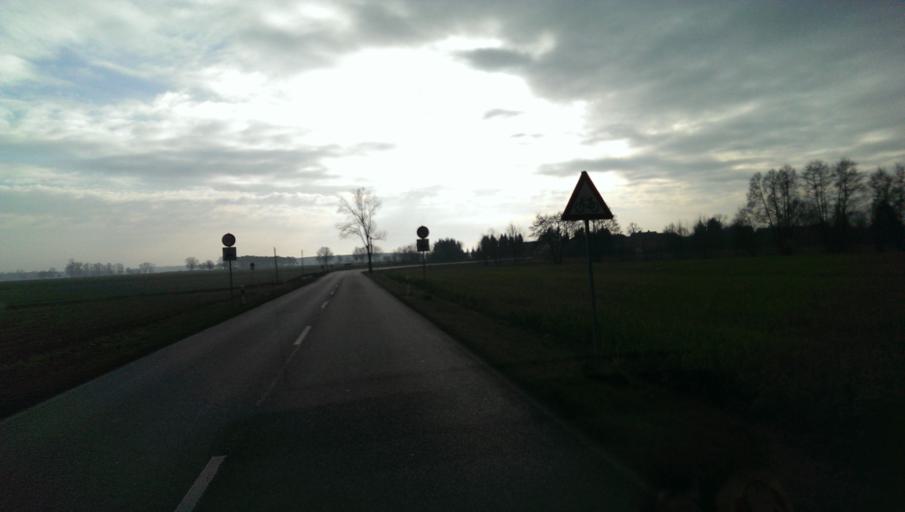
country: DE
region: Saxony-Anhalt
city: Holzdorf
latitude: 51.8220
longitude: 13.1658
